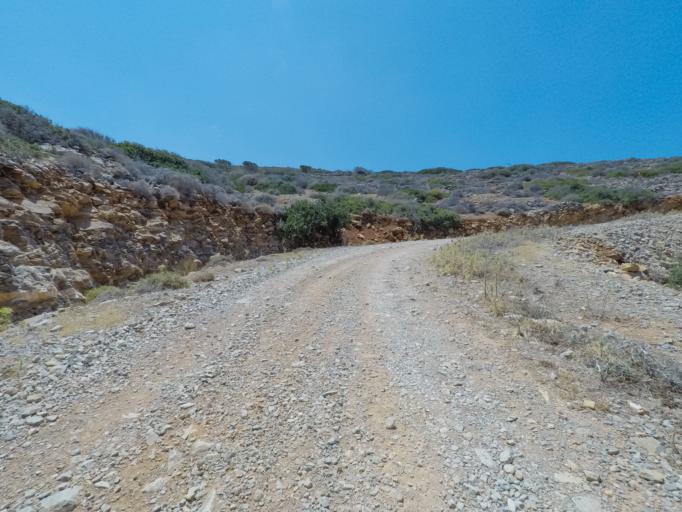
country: GR
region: Crete
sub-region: Nomos Lasithiou
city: Elounda
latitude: 35.3273
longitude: 25.7609
